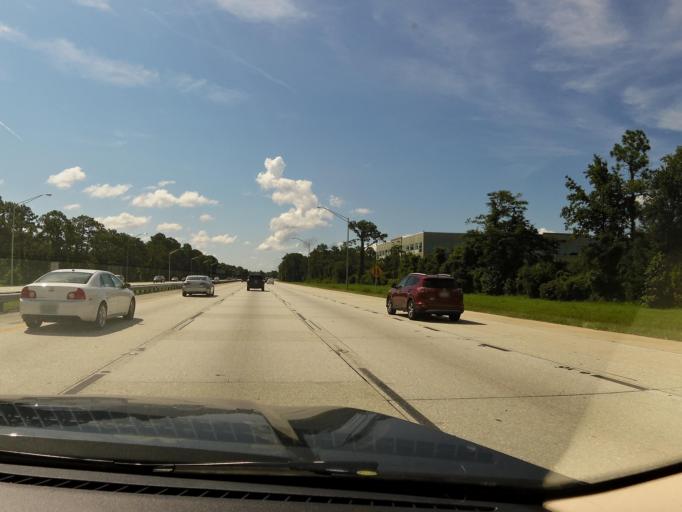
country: US
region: Florida
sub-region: Duval County
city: Jacksonville
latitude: 30.2429
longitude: -81.5898
